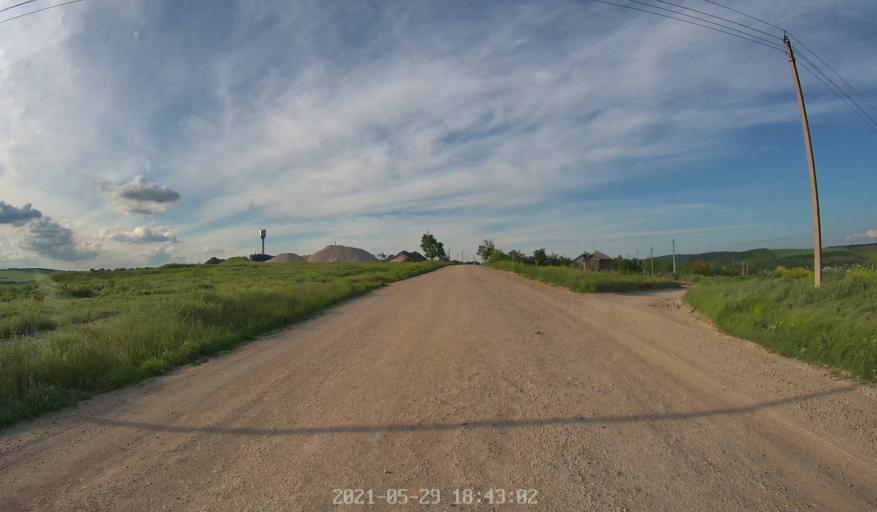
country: MD
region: Chisinau
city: Singera
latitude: 46.8162
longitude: 28.9635
